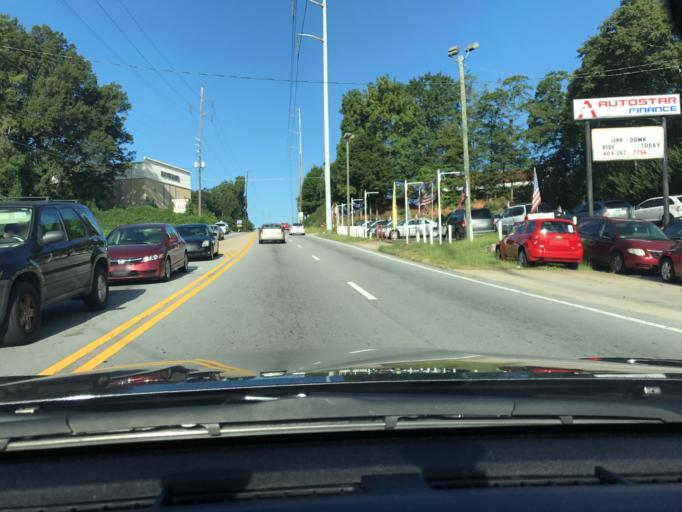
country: US
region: Georgia
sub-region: DeKalb County
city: Scottdale
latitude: 33.7936
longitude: -84.2641
